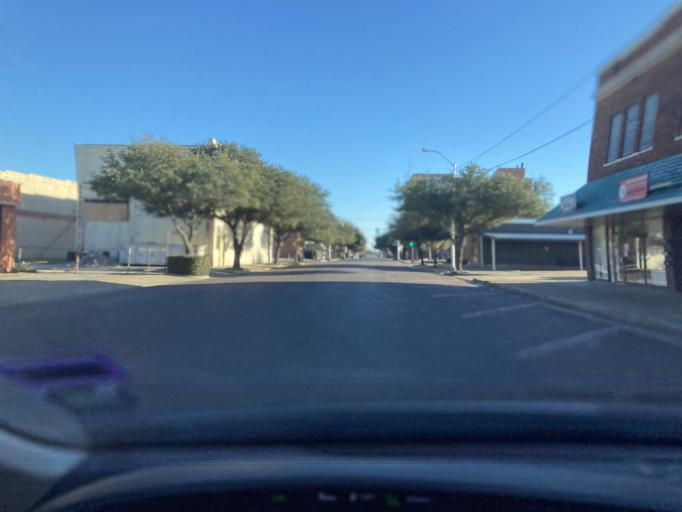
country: US
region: Texas
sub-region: Navarro County
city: Corsicana
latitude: 32.0946
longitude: -96.4659
